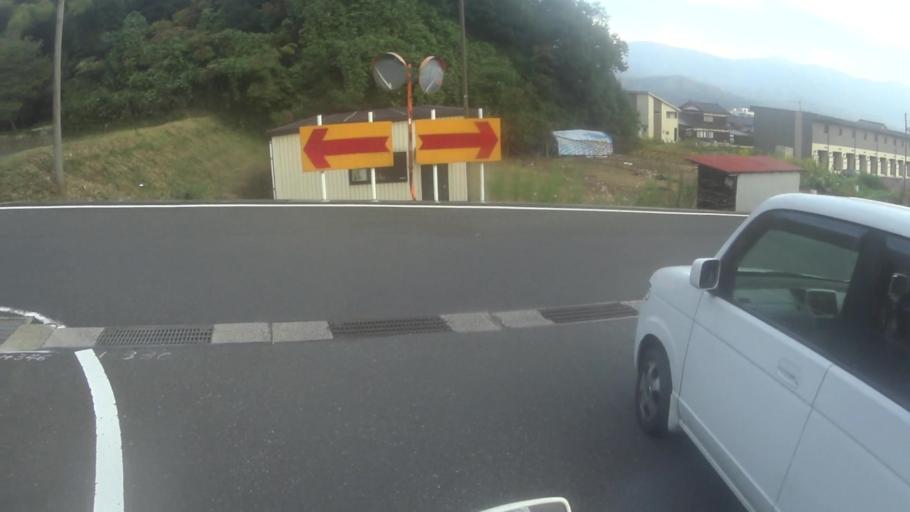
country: JP
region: Kyoto
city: Miyazu
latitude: 35.5250
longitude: 135.0928
